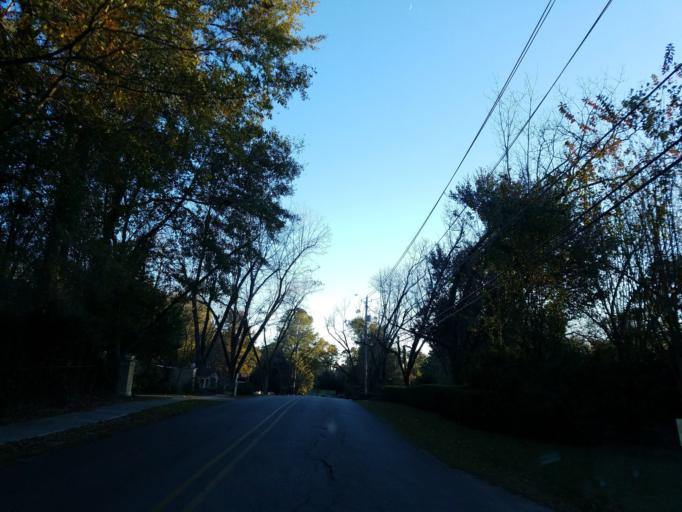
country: US
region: Mississippi
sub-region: Lamar County
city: West Hattiesburg
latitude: 31.3194
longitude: -89.3402
